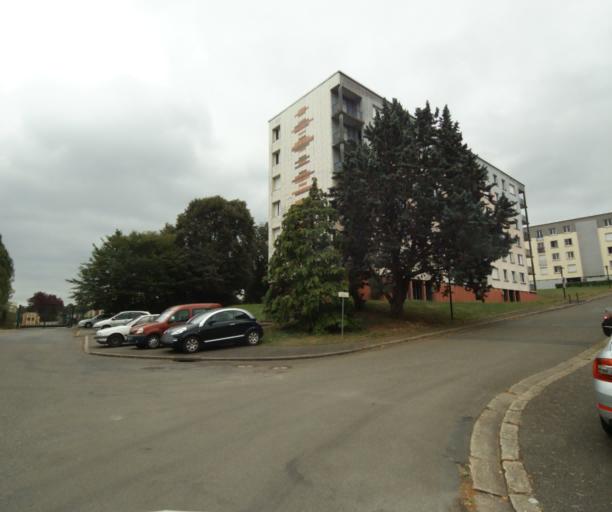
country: FR
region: Pays de la Loire
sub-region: Departement de la Sarthe
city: Solesmes
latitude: 47.8366
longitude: -0.3123
